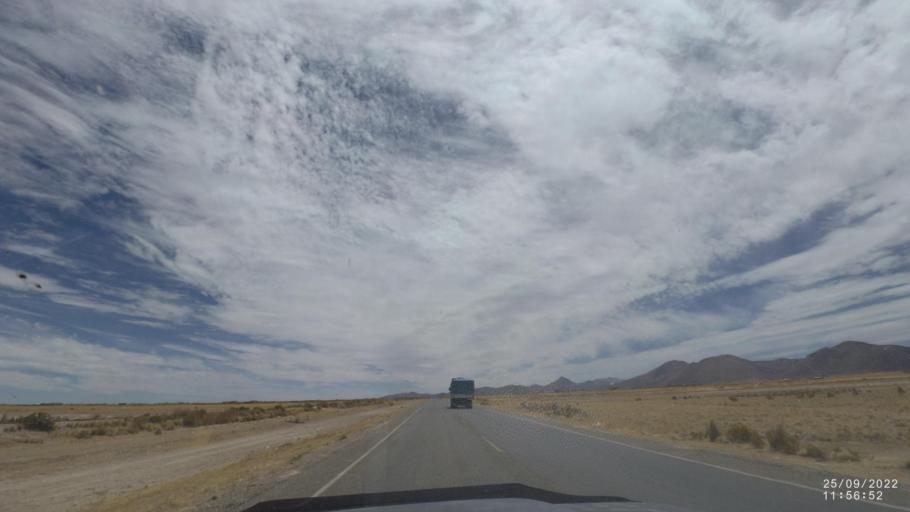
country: BO
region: Oruro
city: Challapata
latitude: -18.8330
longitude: -66.8225
